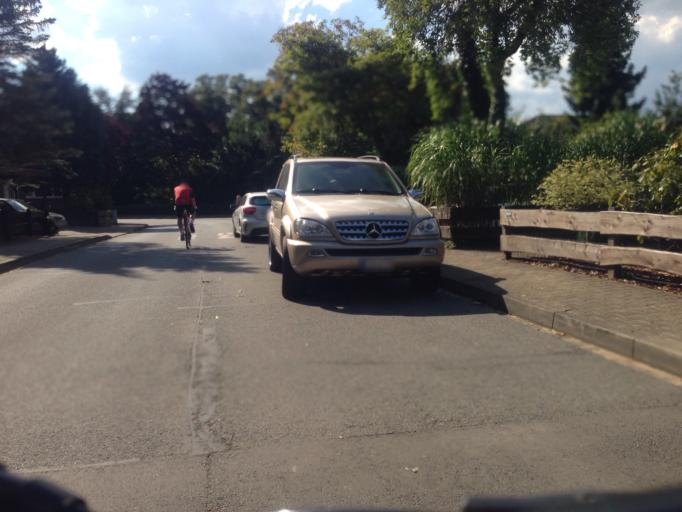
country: DE
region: Lower Saxony
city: Adendorf
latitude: 53.2881
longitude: 10.4466
